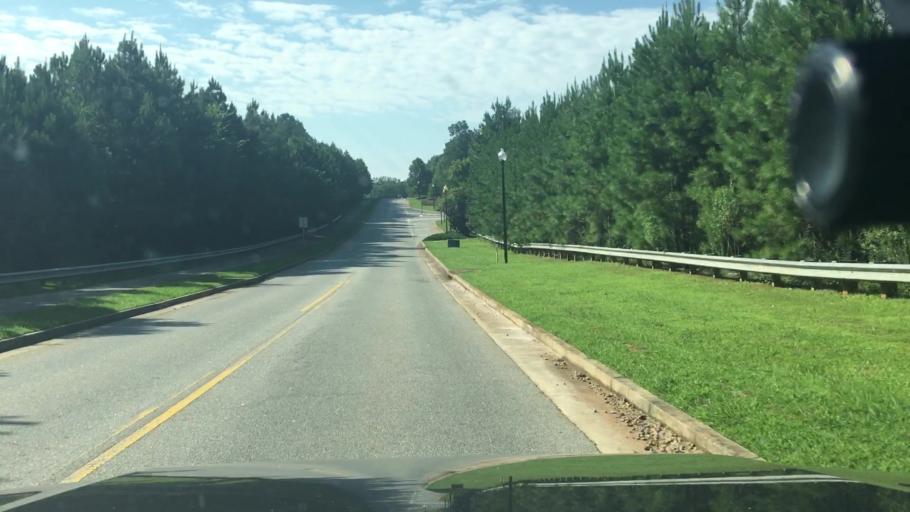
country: US
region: Georgia
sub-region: Coweta County
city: East Newnan
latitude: 33.3677
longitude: -84.7563
